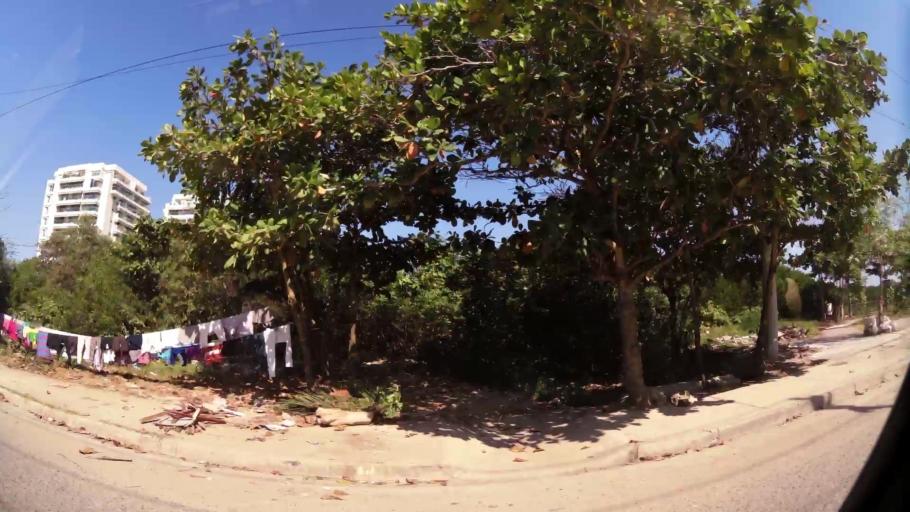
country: CO
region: Bolivar
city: Cartagena
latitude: 10.4371
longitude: -75.5303
